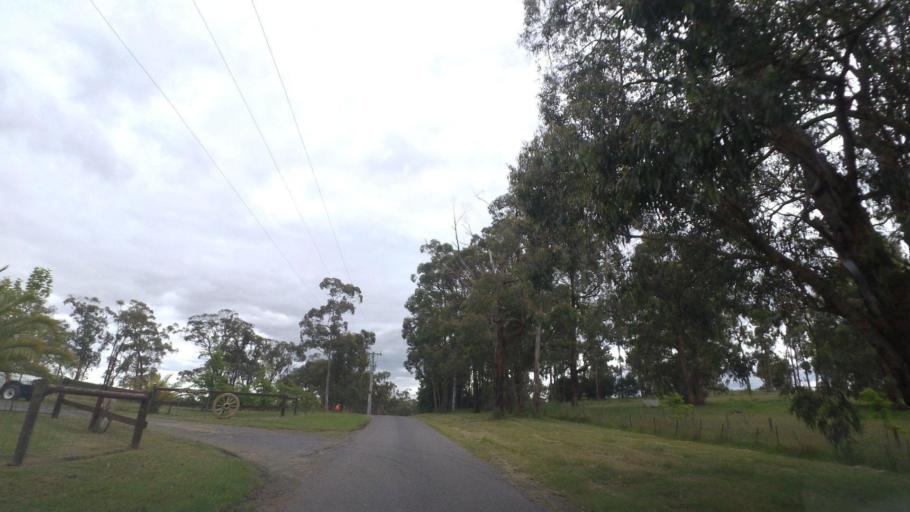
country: AU
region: Victoria
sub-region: Yarra Ranges
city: Mount Evelyn
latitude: -37.7542
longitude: 145.4208
